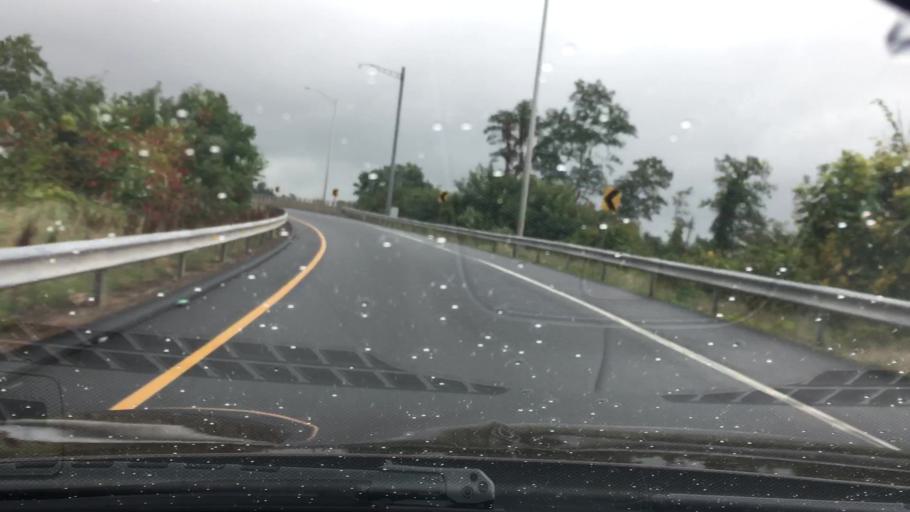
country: US
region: Connecticut
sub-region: Hartford County
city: West Hartford
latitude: 41.7258
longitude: -72.7709
